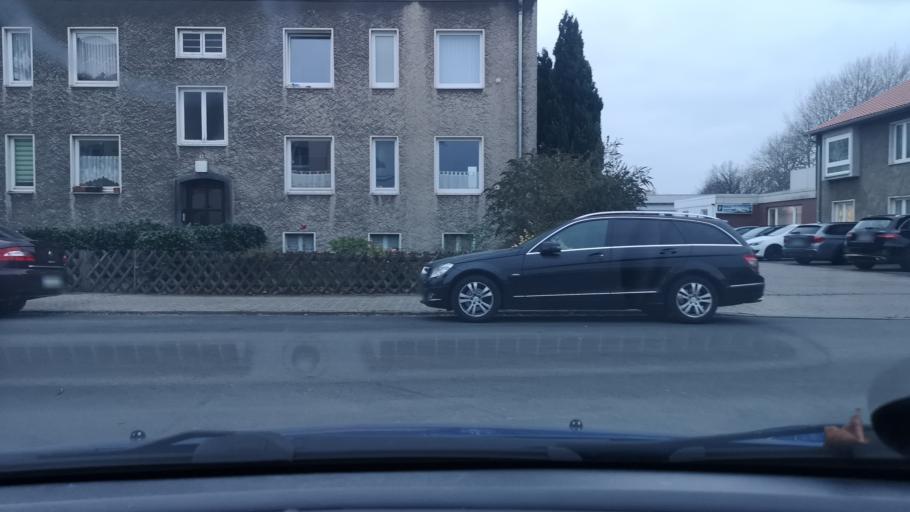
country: DE
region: Lower Saxony
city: Langenhagen
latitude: 52.4567
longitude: 9.7307
